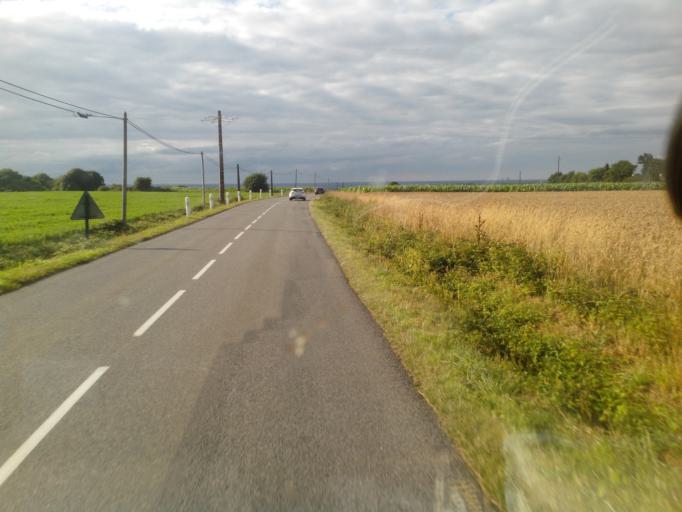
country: FR
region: Brittany
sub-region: Departement d'Ille-et-Vilaine
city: Paimpont
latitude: 48.0398
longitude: -2.1826
